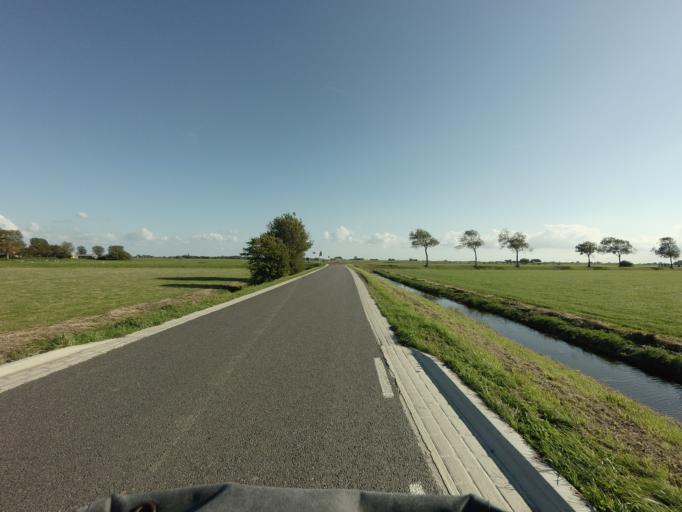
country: NL
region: Friesland
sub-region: Sudwest Fryslan
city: Bolsward
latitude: 53.0343
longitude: 5.5055
